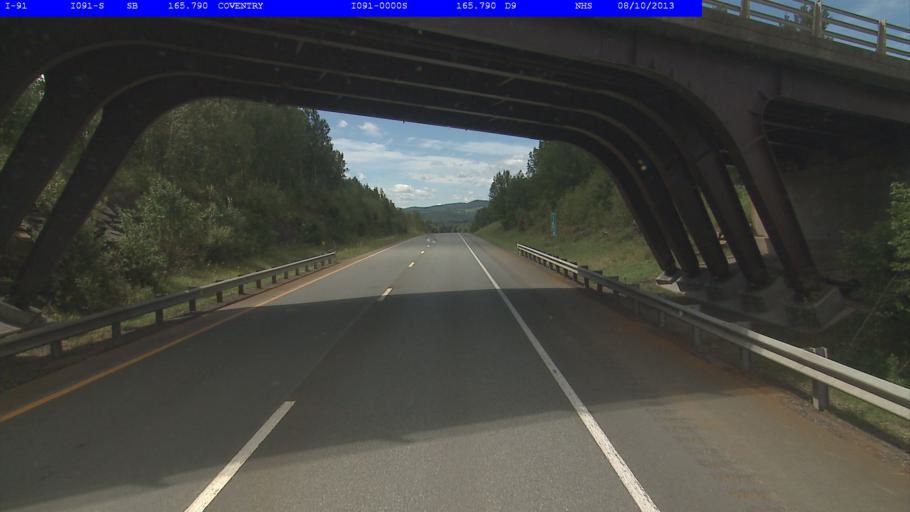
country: US
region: Vermont
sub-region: Orleans County
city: Newport
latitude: 44.8647
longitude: -72.1853
